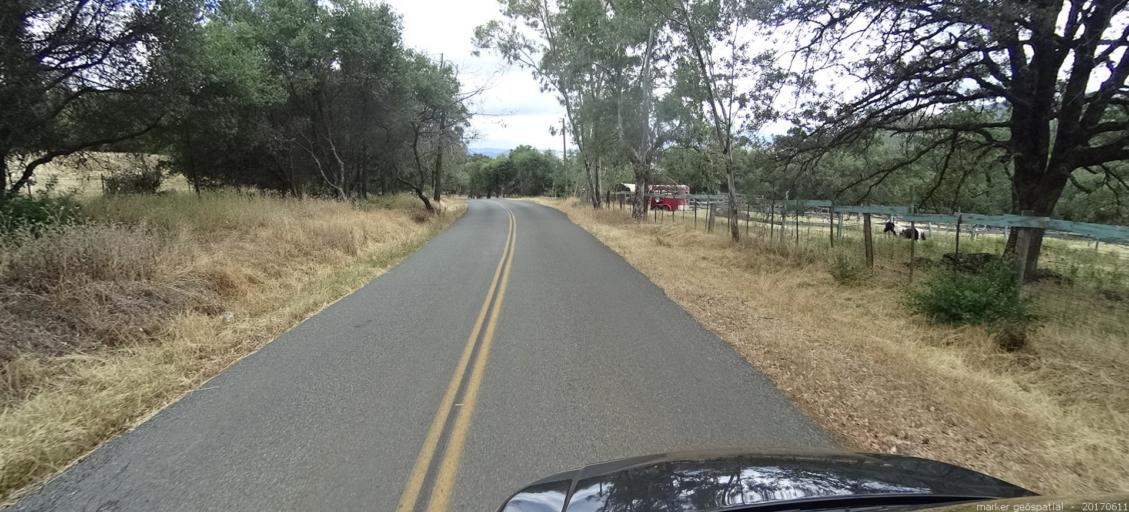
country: US
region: California
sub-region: Butte County
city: Oroville
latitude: 39.6343
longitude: -121.5281
